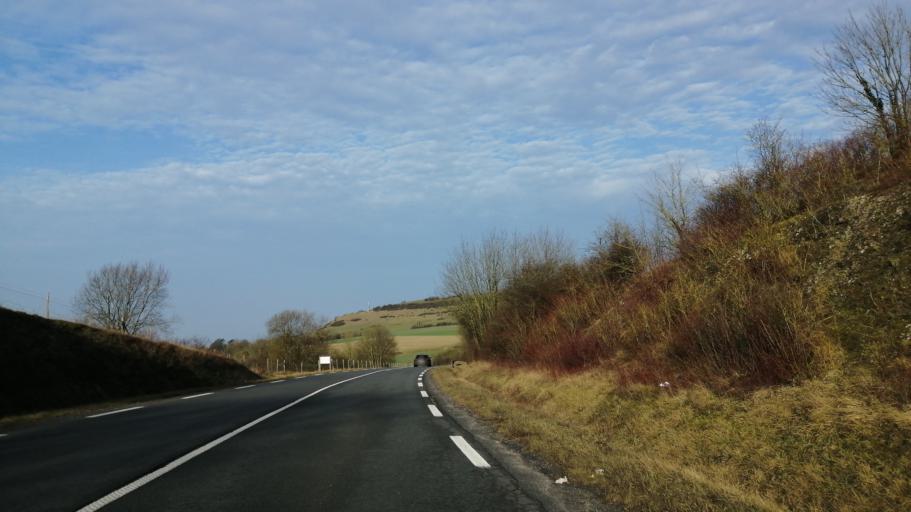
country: FR
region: Nord-Pas-de-Calais
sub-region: Departement du Pas-de-Calais
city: Licques
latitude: 50.7302
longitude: 1.8961
